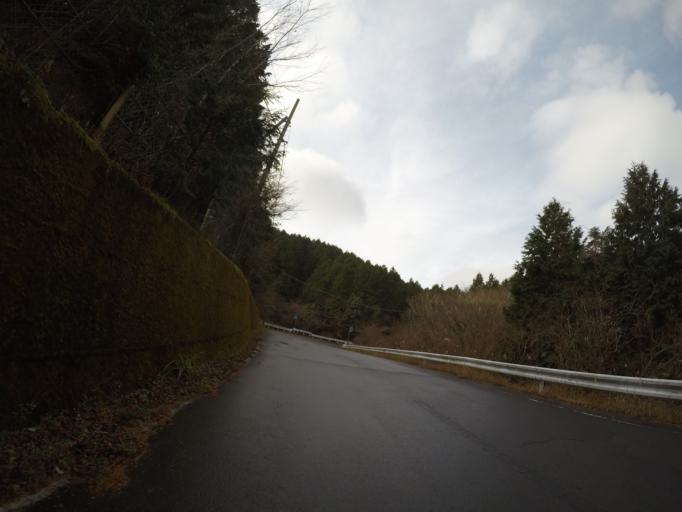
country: JP
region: Shizuoka
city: Heda
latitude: 34.8744
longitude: 138.8506
